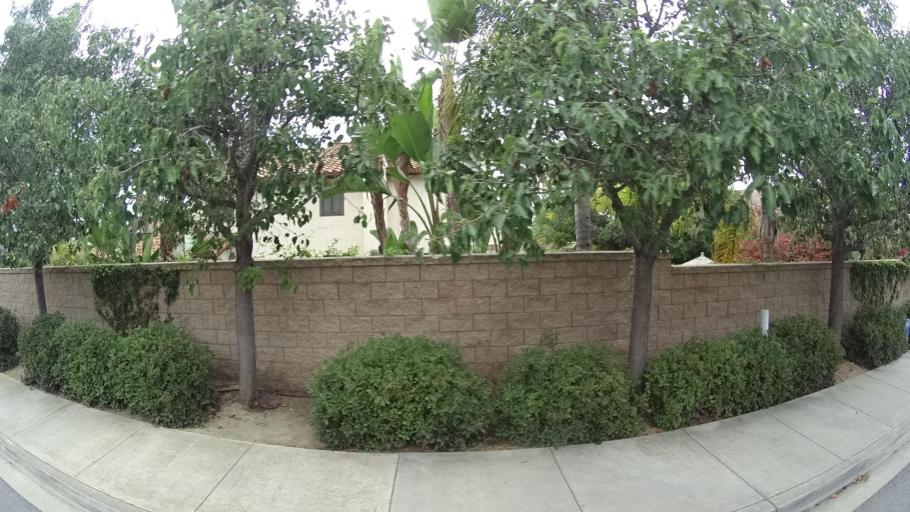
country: US
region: California
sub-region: San Diego County
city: Escondido
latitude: 33.1516
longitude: -117.1104
